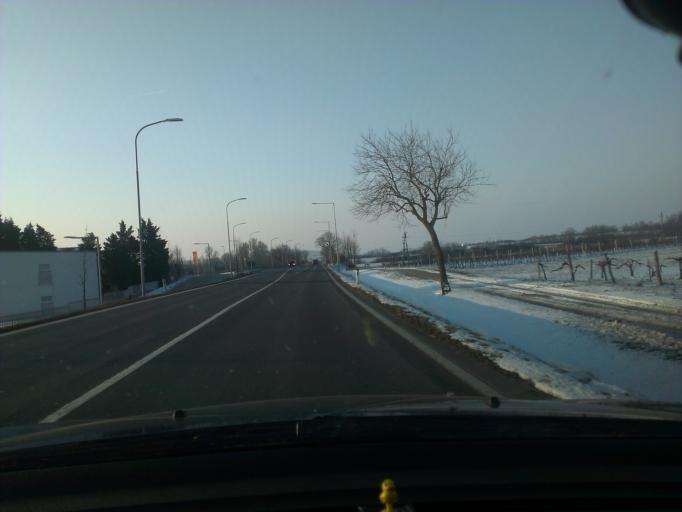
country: AT
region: Burgenland
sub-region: Eisenstadt-Umgebung
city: Donnerskirchen
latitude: 47.8750
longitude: 16.6494
